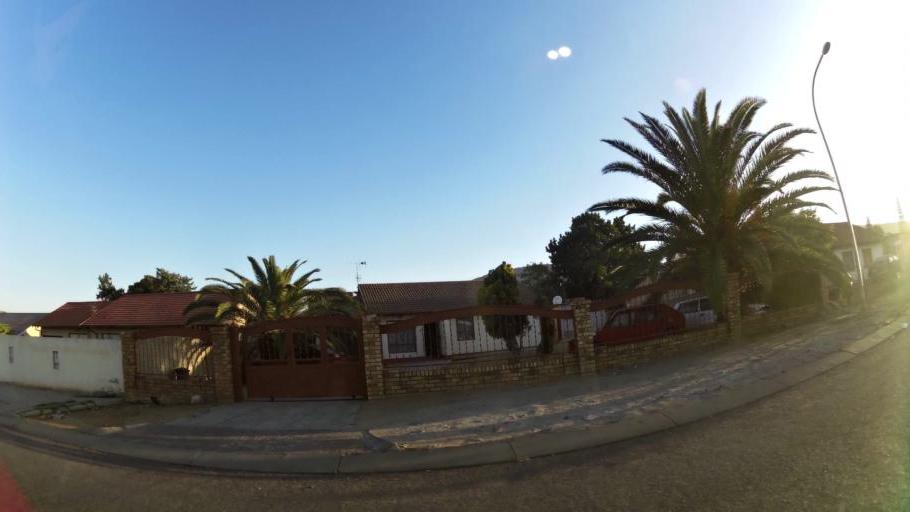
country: ZA
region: North-West
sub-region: Bojanala Platinum District Municipality
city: Rustenburg
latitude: -25.6383
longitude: 27.2050
